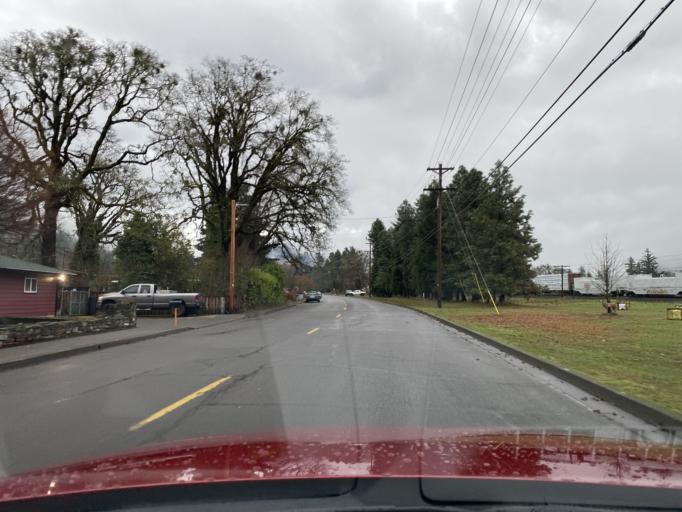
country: US
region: Oregon
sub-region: Lane County
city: Oakridge
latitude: 43.7476
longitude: -122.4777
